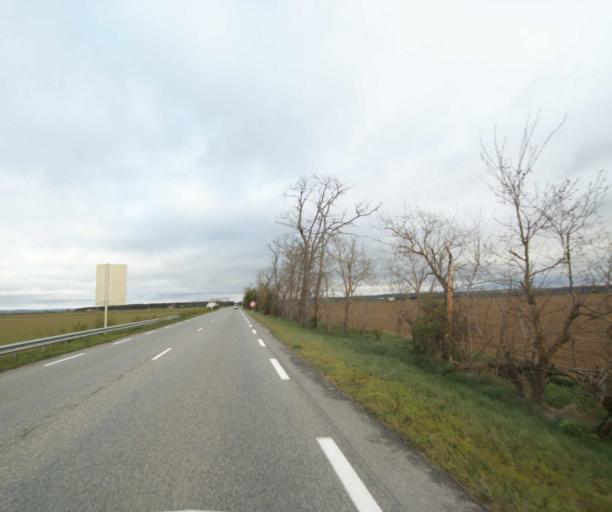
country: FR
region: Midi-Pyrenees
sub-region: Departement de l'Ariege
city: Saverdun
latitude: 43.2616
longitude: 1.5586
